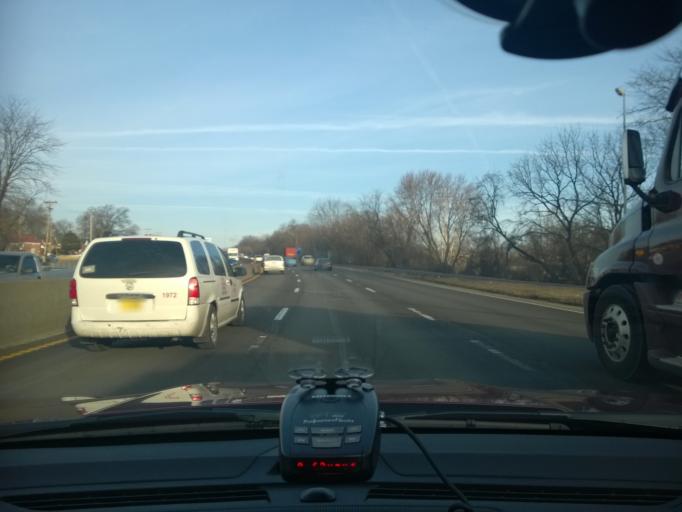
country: US
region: Missouri
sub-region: Saint Louis County
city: Pine Lawn
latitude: 38.7059
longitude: -90.2723
